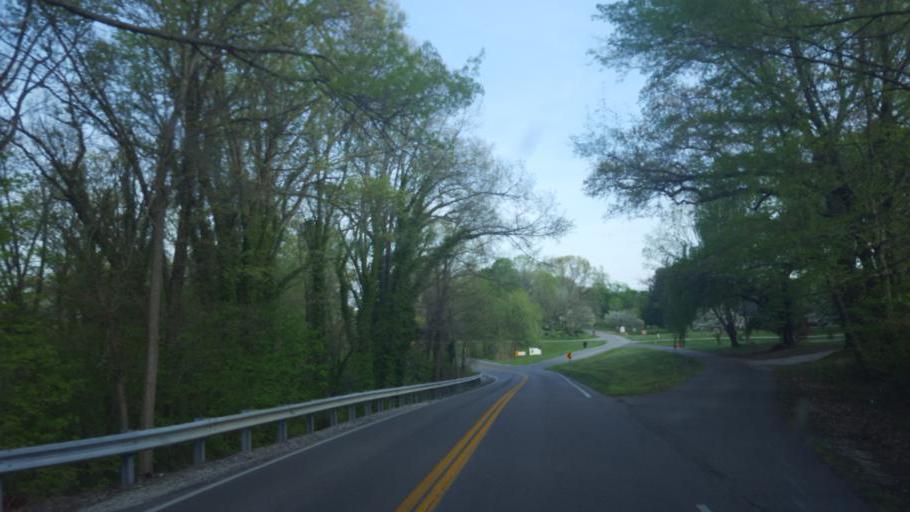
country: US
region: Kentucky
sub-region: Warren County
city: Plano
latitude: 36.9446
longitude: -86.3316
